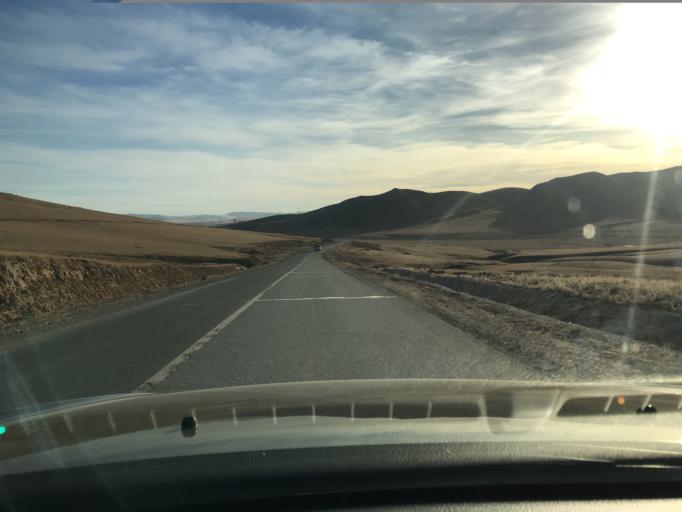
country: MN
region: Central Aimak
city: Dzuunmod
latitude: 47.8099
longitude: 107.3266
